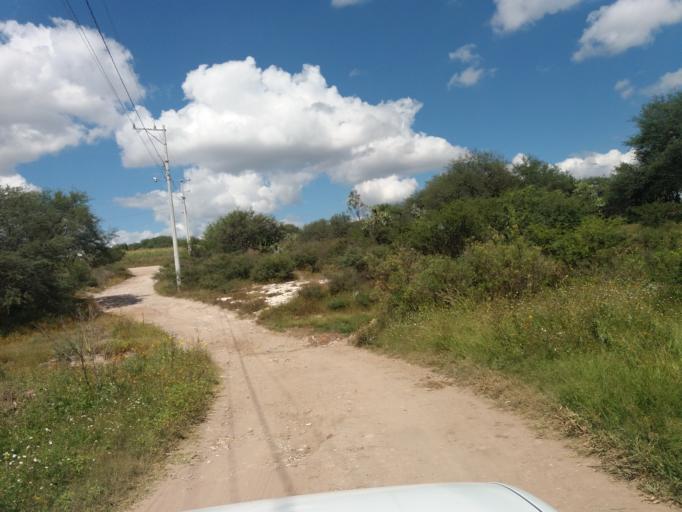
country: MX
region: Aguascalientes
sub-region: Aguascalientes
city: San Sebastian [Fraccionamiento]
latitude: 21.8080
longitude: -102.2415
